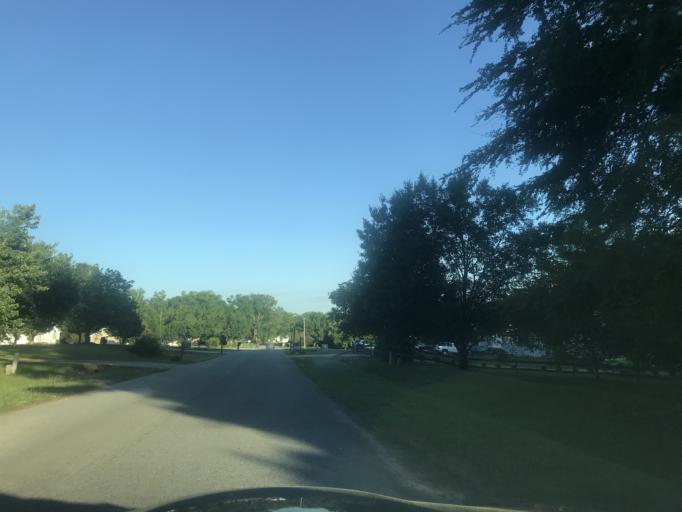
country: US
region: North Carolina
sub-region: Johnston County
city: Archer Lodge
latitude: 35.6848
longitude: -78.3439
